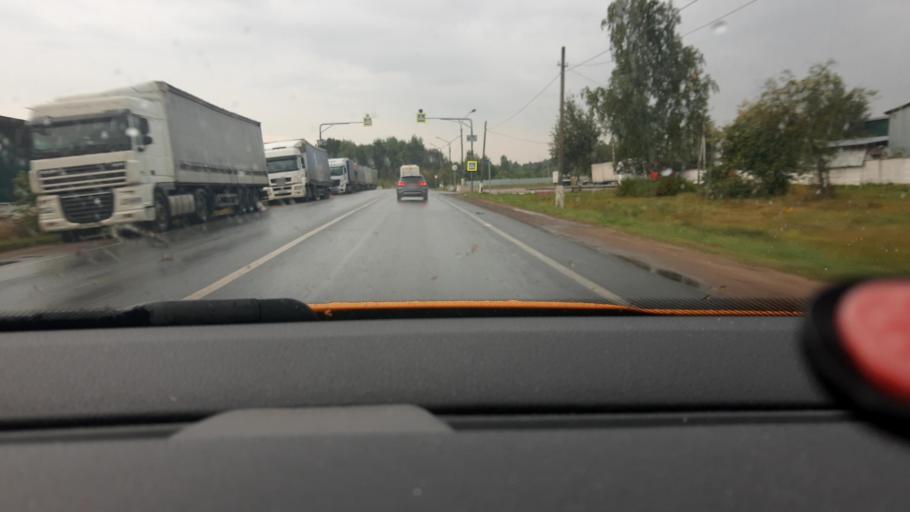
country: RU
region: Moskovskaya
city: Obukhovo
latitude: 55.8201
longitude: 38.2607
